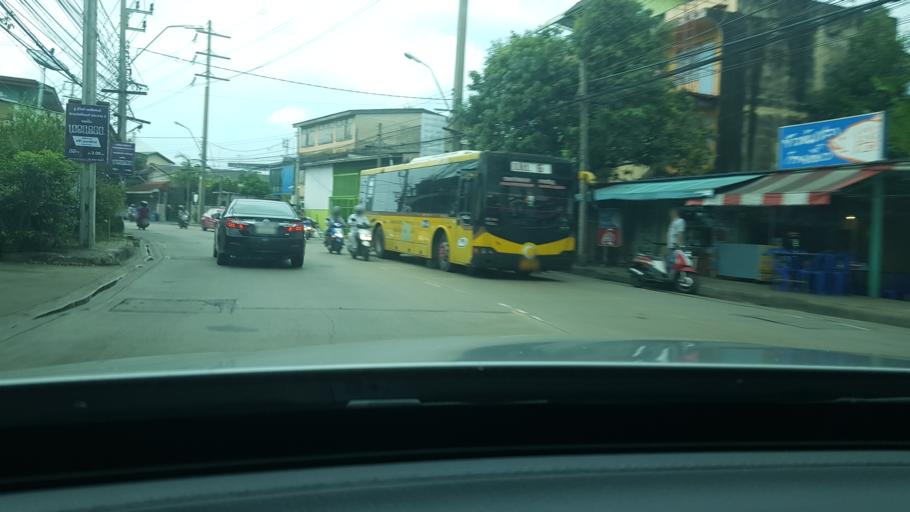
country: TH
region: Samut Prakan
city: Phra Pradaeng
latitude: 13.6663
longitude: 100.5250
